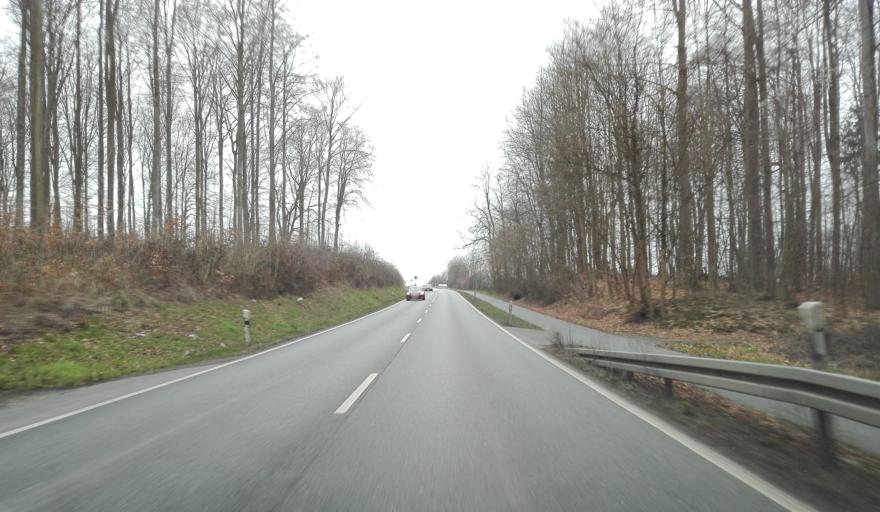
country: DE
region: Hesse
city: Ober-Ramstadt
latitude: 49.8177
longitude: 8.7670
